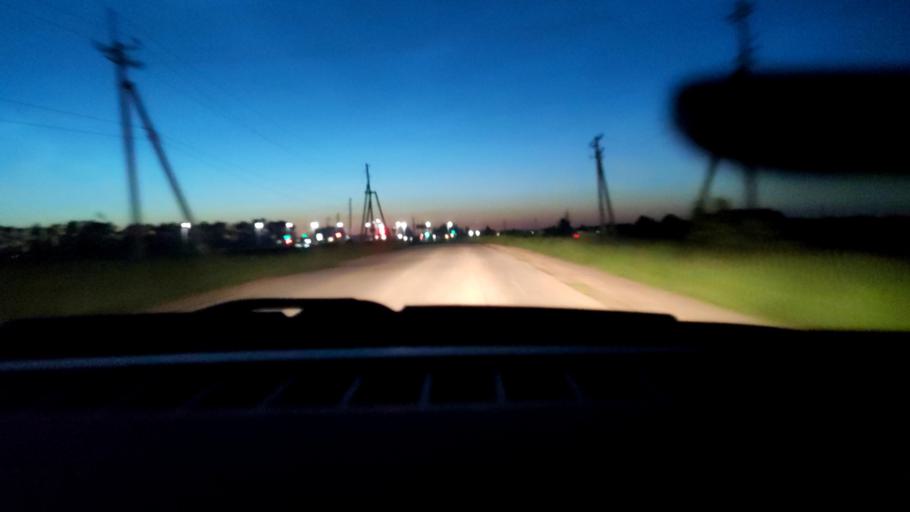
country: RU
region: Perm
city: Kultayevo
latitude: 57.8817
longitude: 55.9228
